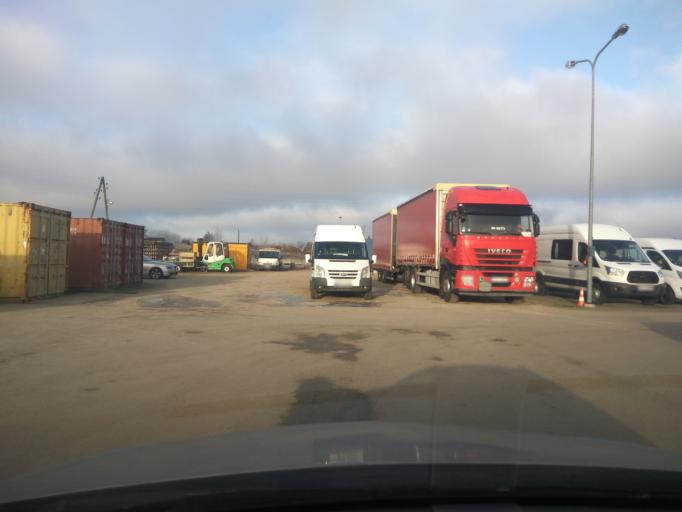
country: LV
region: Kuldigas Rajons
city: Kuldiga
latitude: 56.9664
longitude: 21.9340
